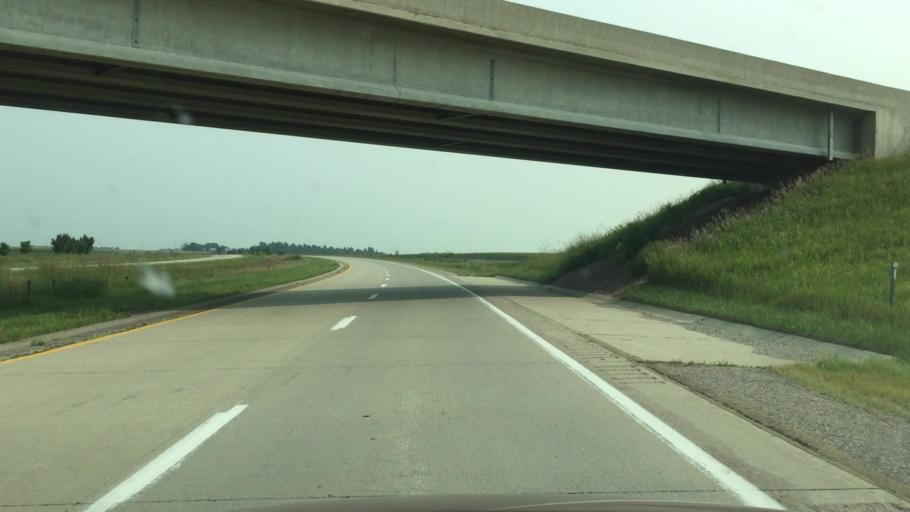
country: US
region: Iowa
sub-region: Osceola County
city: Sibley
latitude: 43.3894
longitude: -95.7200
